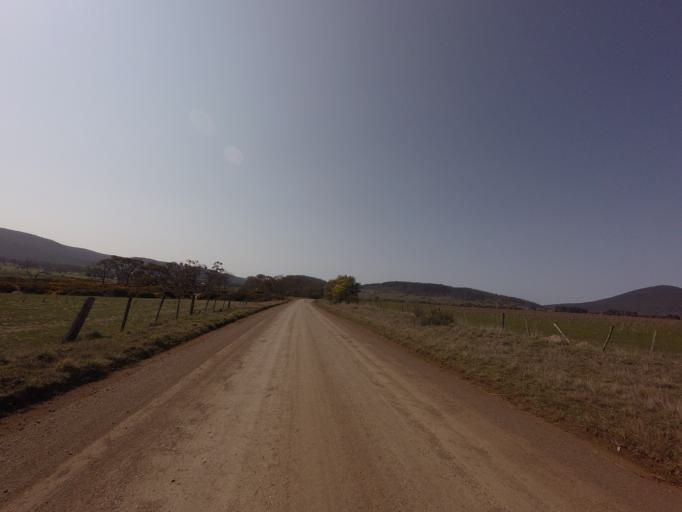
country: AU
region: Tasmania
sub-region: Break O'Day
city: St Helens
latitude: -41.8172
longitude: 147.9373
